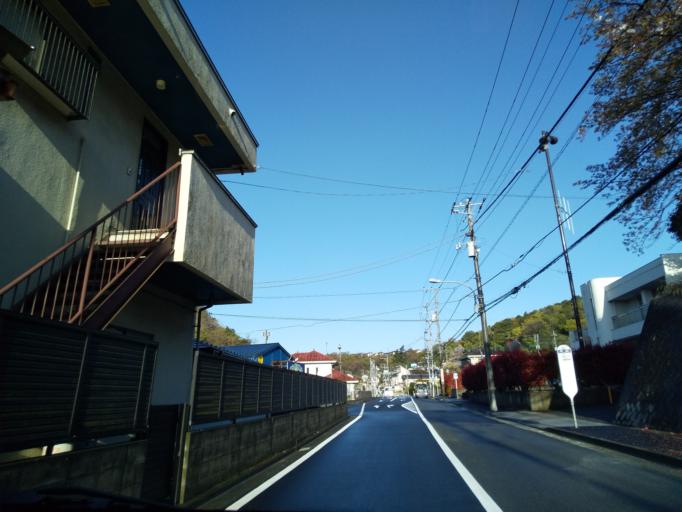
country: JP
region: Tokyo
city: Hachioji
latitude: 35.6276
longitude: 139.3635
